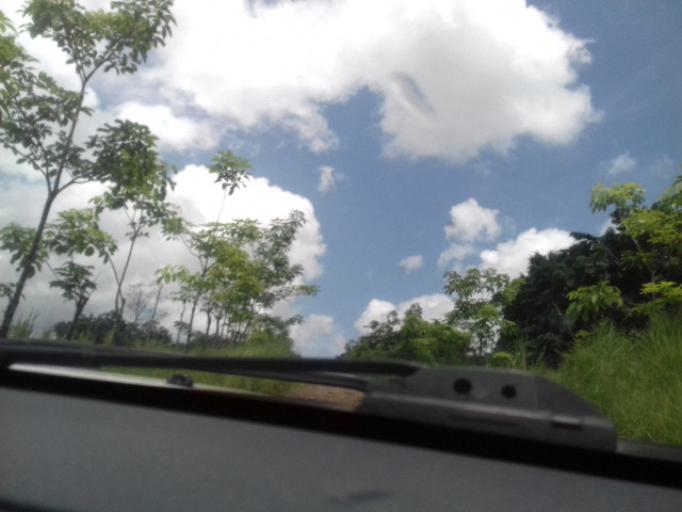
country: NI
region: Matagalpa
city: Rio Blanco
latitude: 12.9997
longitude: -85.3872
